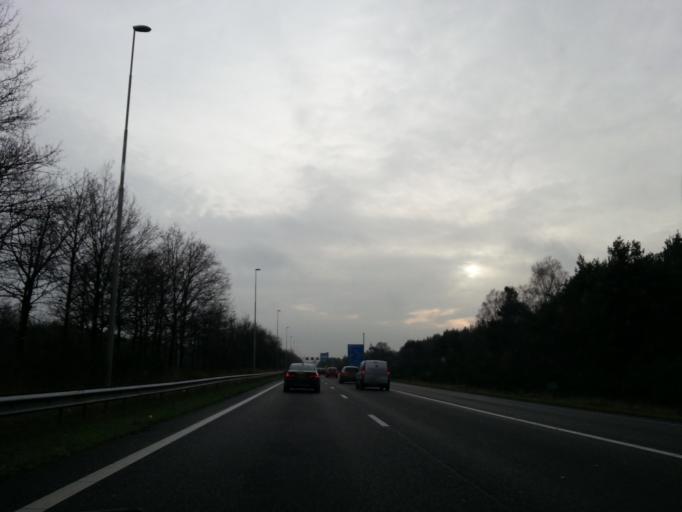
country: NL
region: Gelderland
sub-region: Gemeente Rozendaal
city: Rozendaal
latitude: 52.0542
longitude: 5.9382
